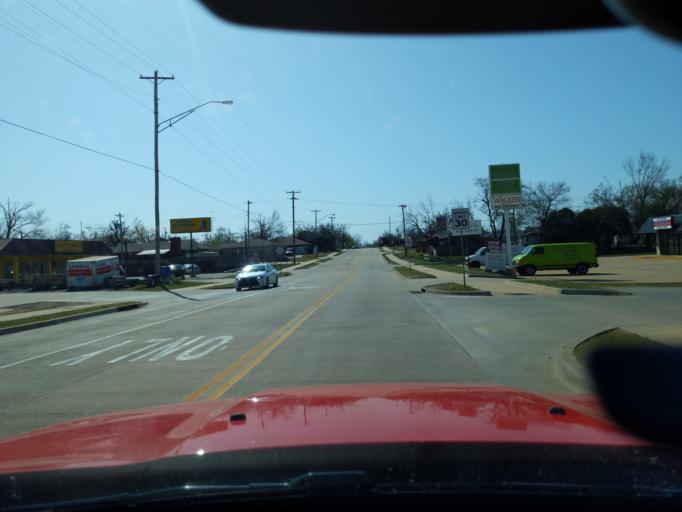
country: US
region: Oklahoma
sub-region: Cleveland County
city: Moore
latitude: 35.3485
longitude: -97.4906
